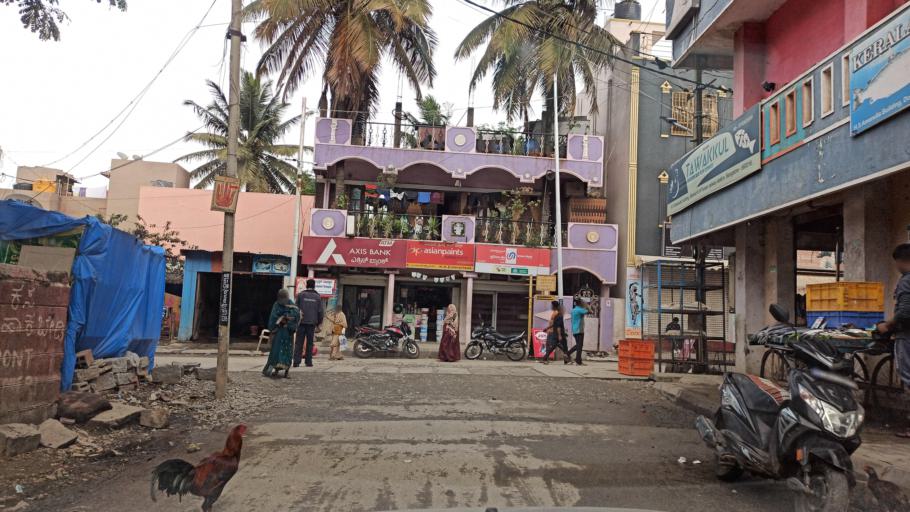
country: IN
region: Karnataka
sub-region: Bangalore Urban
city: Bangalore
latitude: 13.0022
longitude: 77.6755
